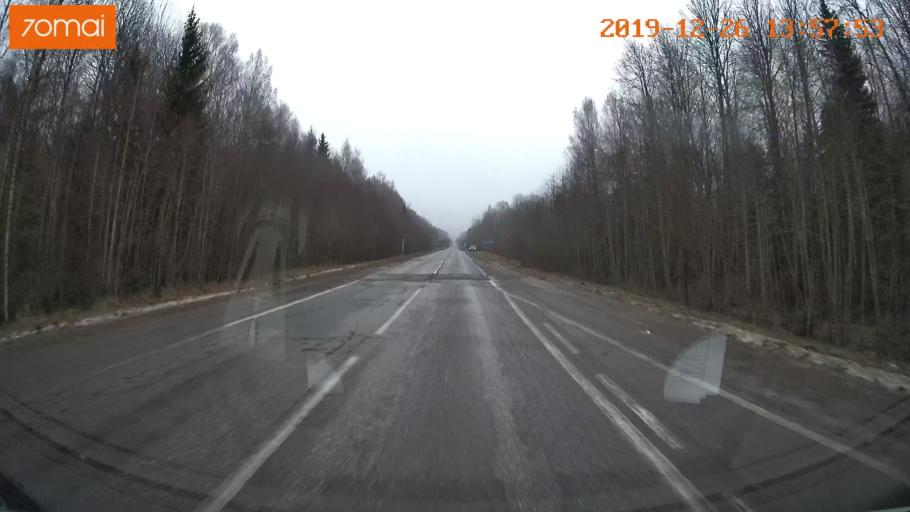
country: RU
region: Jaroslavl
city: Poshekhon'ye
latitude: 58.5786
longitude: 38.6888
